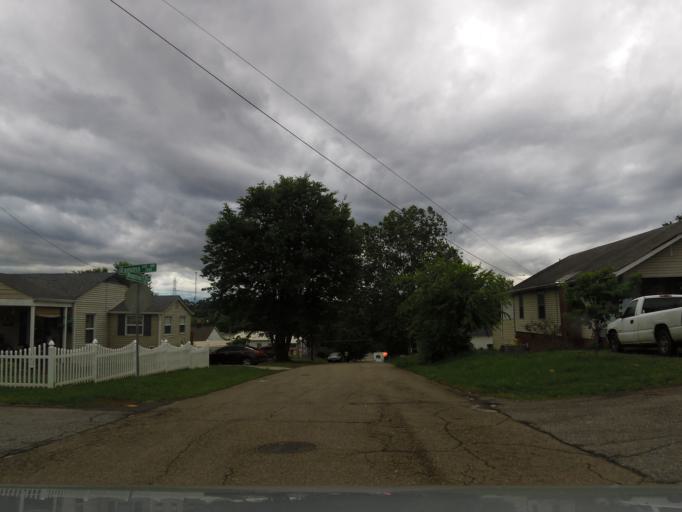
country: US
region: Tennessee
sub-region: Knox County
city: Knoxville
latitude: 35.9652
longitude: -83.9607
